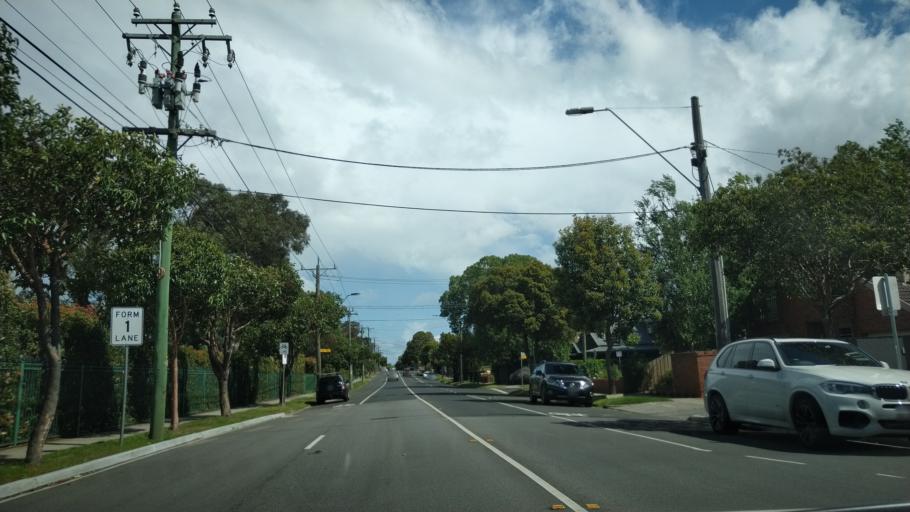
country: AU
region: Victoria
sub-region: Stonnington
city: Malvern East
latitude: -37.8778
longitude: 145.0353
